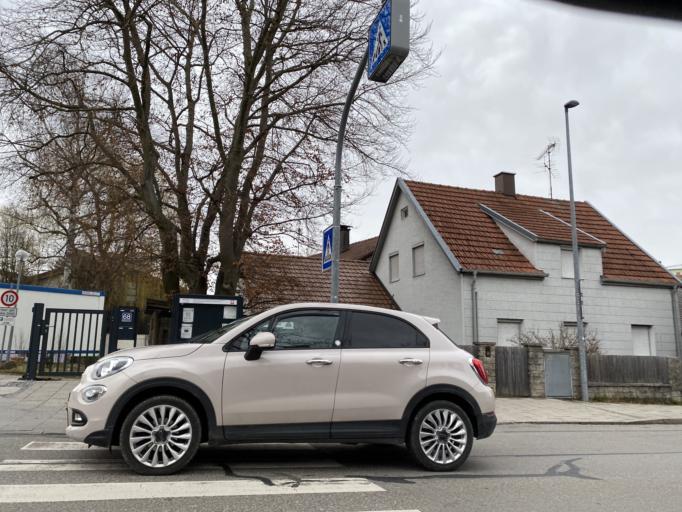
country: DE
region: Bavaria
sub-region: Upper Bavaria
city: Fuerstenfeldbruck
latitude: 48.1863
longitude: 11.2550
